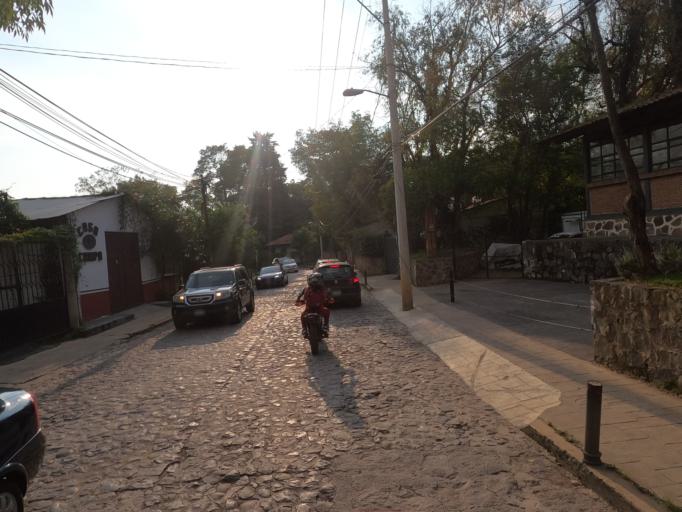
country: MX
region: Mexico
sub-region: Valle de Bravo
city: Colonia Rincon Villa del Valle
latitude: 19.2049
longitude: -100.1225
